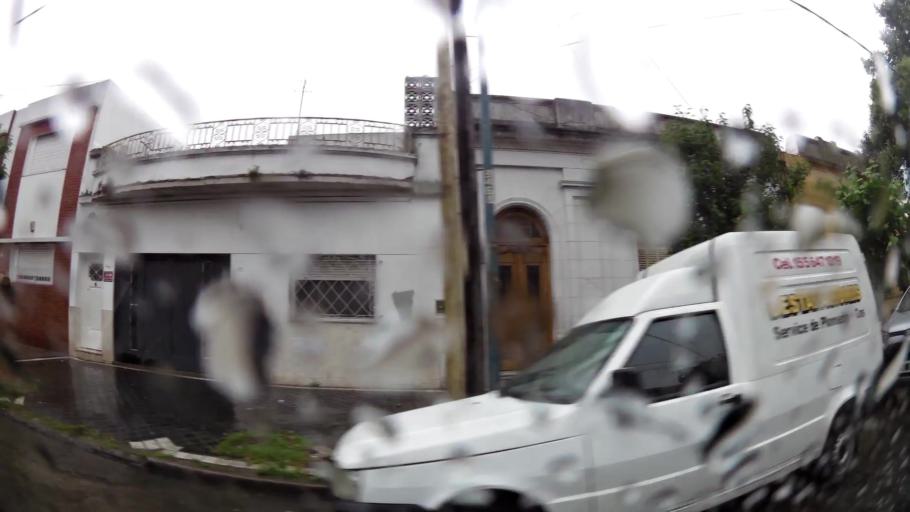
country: AR
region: Buenos Aires
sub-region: Partido de Lanus
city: Lanus
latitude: -34.7131
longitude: -58.3950
